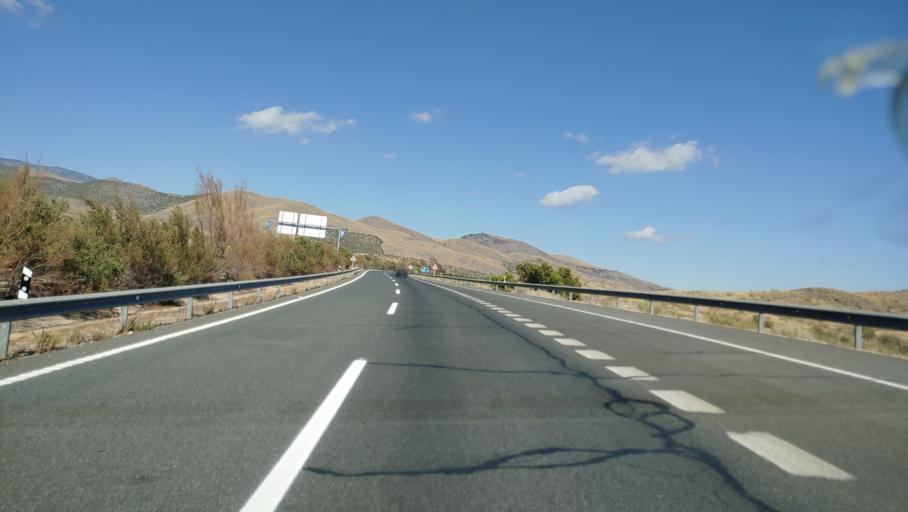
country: ES
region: Andalusia
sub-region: Provincia de Almeria
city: Gergal
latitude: 37.1179
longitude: -2.5882
